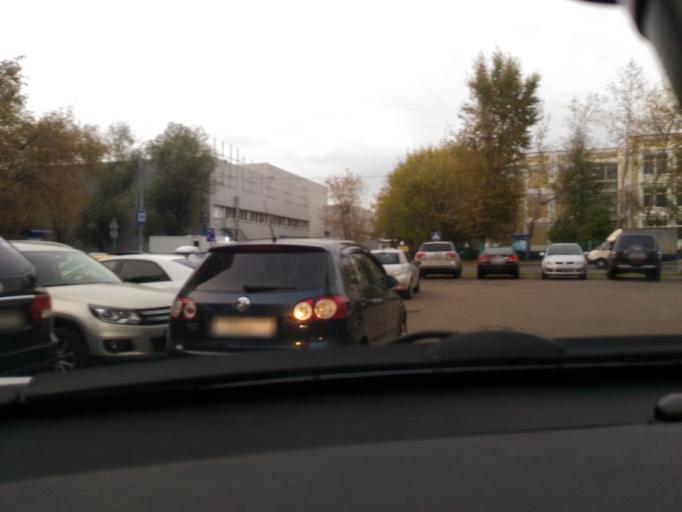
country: RU
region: Moscow
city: Vatutino
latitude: 55.8737
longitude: 37.6717
